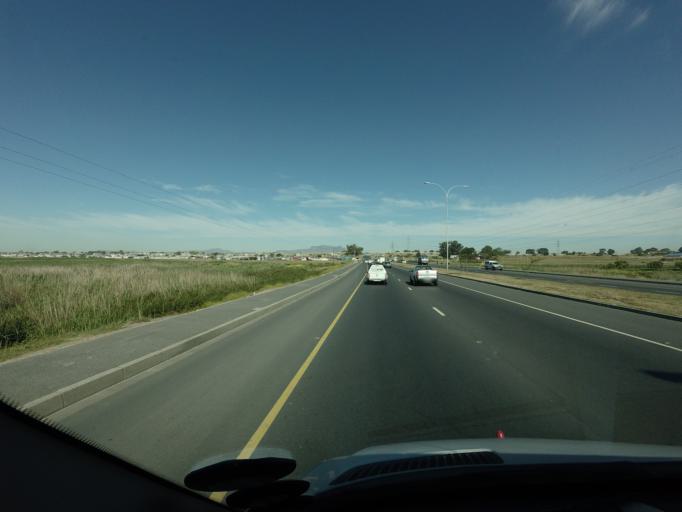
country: ZA
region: Western Cape
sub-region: City of Cape Town
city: Kraaifontein
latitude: -33.9551
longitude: 18.6626
